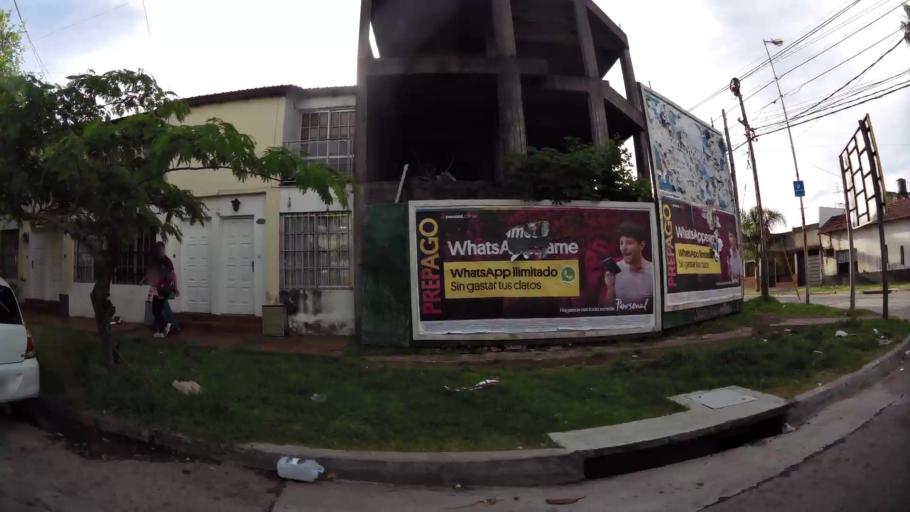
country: AR
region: Buenos Aires
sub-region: Partido de Moron
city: Moron
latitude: -34.6594
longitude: -58.6187
